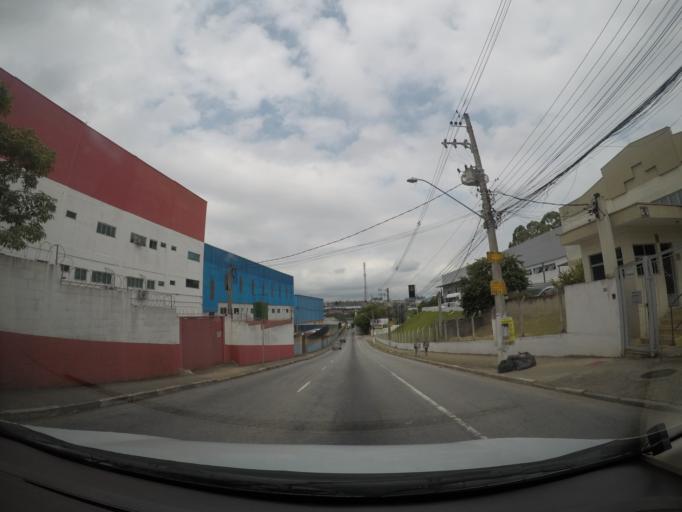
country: BR
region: Sao Paulo
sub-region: Itaquaquecetuba
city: Itaquaquecetuba
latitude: -23.4333
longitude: -46.4087
